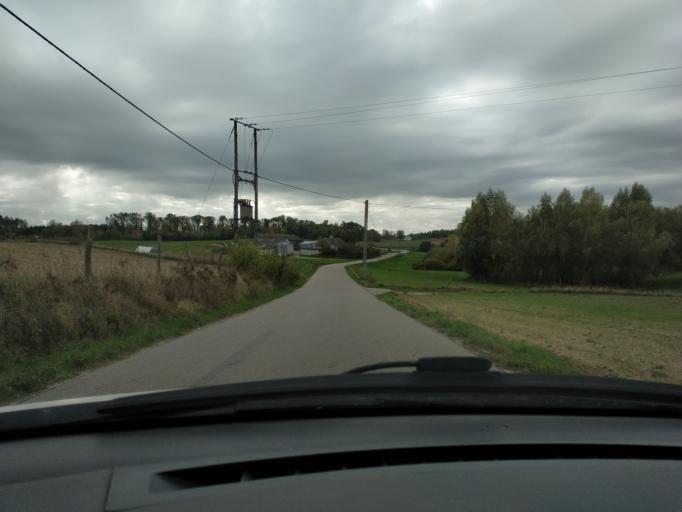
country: PL
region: Warmian-Masurian Voivodeship
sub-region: Powiat nowomiejski
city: Biskupiec
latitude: 53.4594
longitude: 19.3180
